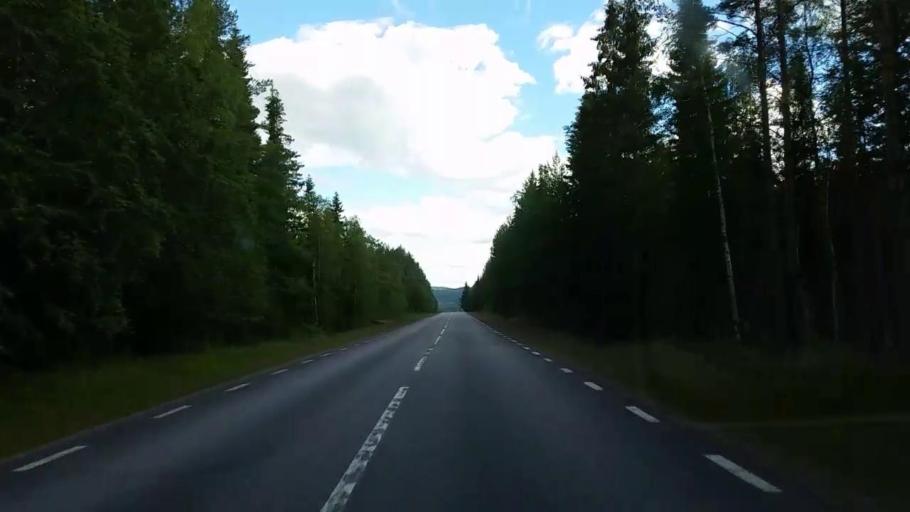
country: SE
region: Gaevleborg
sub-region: Ljusdals Kommun
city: Farila
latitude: 62.1427
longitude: 15.6869
